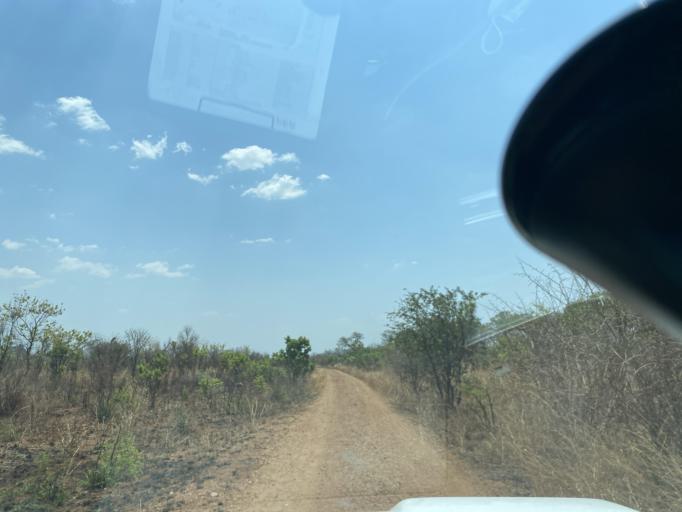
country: ZM
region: Lusaka
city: Lusaka
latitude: -15.5070
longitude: 27.9794
